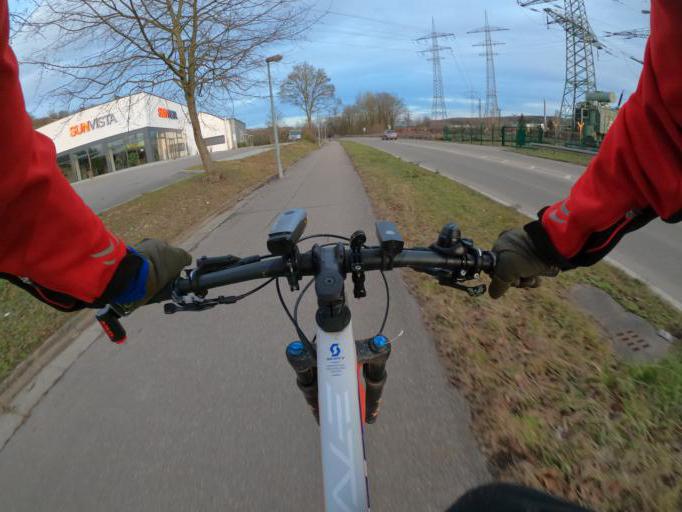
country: DE
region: Baden-Wuerttemberg
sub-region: Regierungsbezirk Stuttgart
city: Deizisau
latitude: 48.7197
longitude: 9.3916
